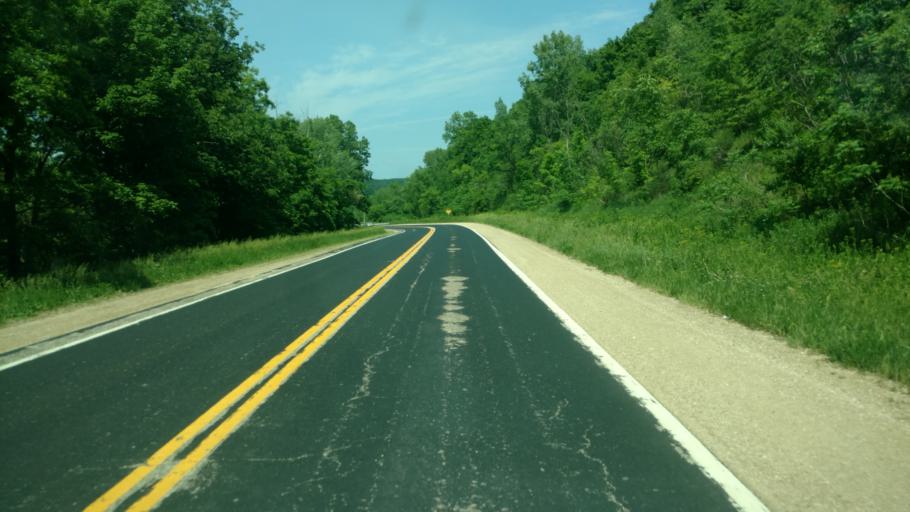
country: US
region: Wisconsin
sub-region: Monroe County
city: Cashton
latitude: 43.5651
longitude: -90.6384
